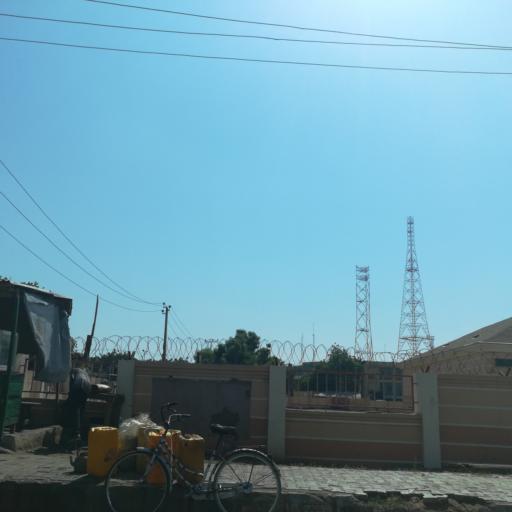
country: NG
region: Kano
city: Kano
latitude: 12.0050
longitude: 8.5373
